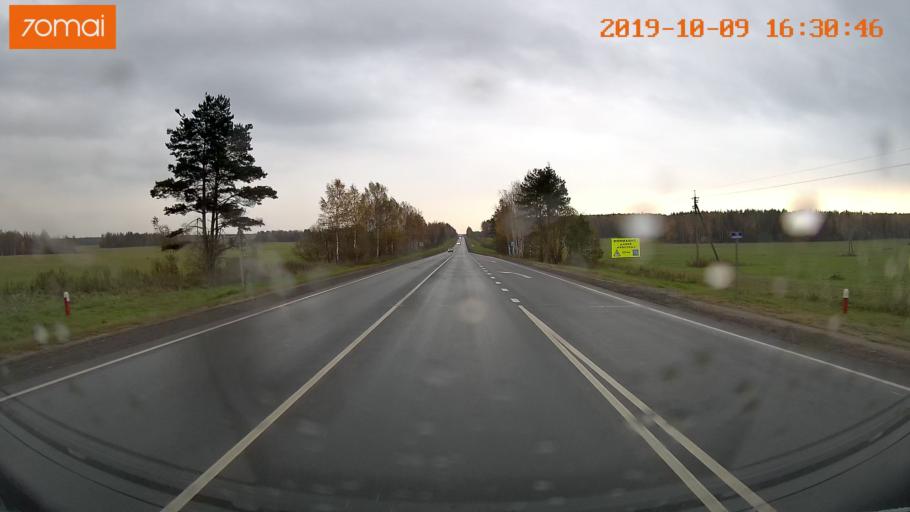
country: RU
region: Kostroma
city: Oktyabr'skiy
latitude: 57.6149
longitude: 40.9440
